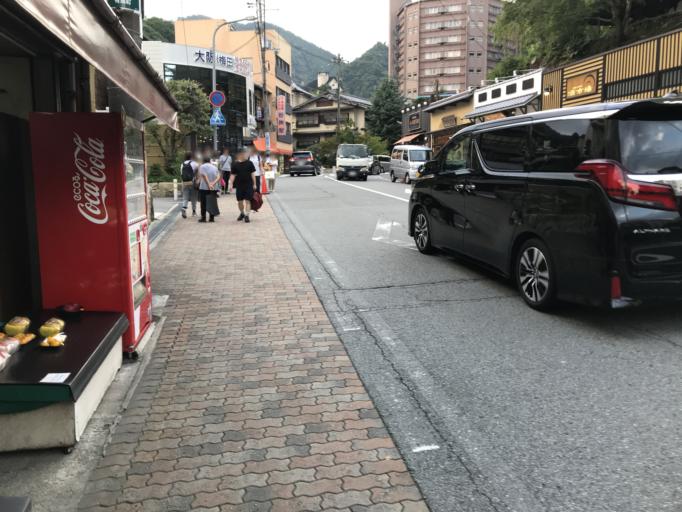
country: JP
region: Hyogo
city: Ashiya
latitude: 34.7976
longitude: 135.2474
